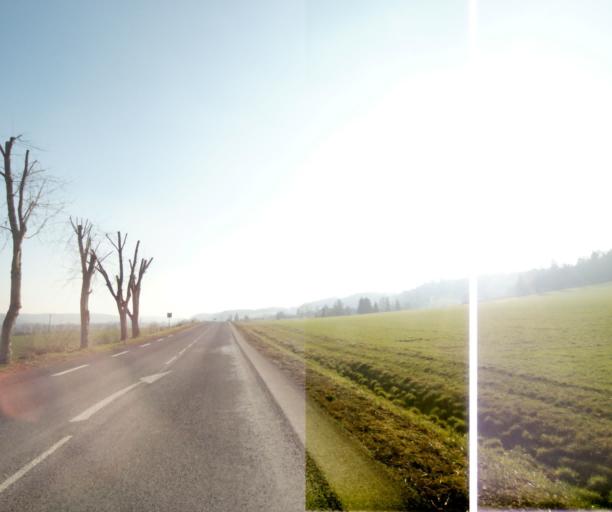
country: FR
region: Champagne-Ardenne
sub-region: Departement de la Haute-Marne
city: Chevillon
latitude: 48.5118
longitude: 5.1118
